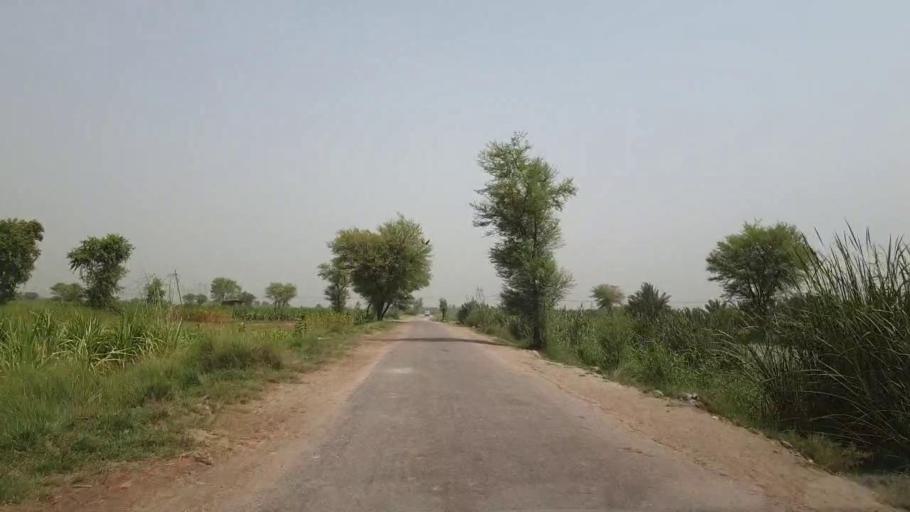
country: PK
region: Sindh
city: Gambat
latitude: 27.4074
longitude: 68.5504
